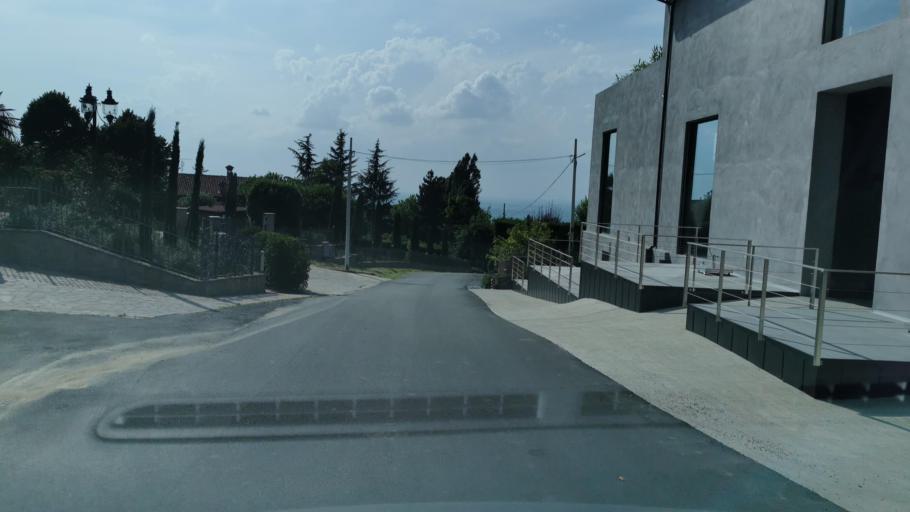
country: IT
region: Piedmont
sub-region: Provincia di Cuneo
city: La Morra
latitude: 44.6435
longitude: 7.9298
